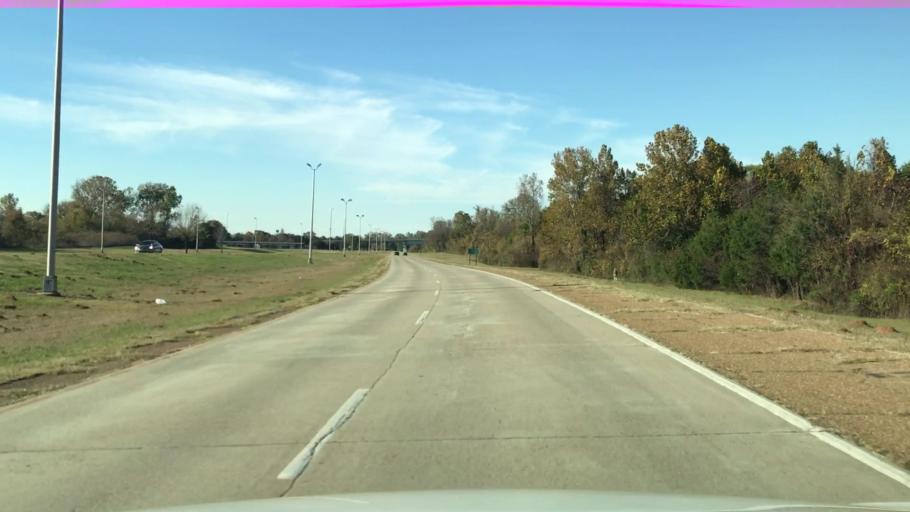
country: US
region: Louisiana
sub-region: Bossier Parish
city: Bossier City
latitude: 32.4853
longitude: -93.6946
